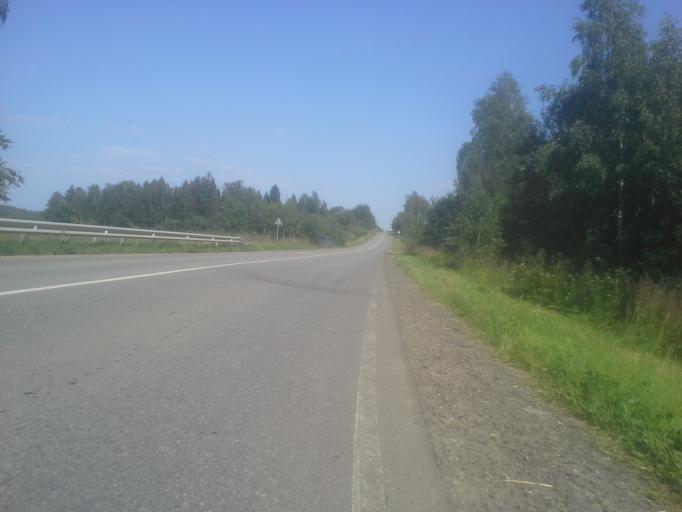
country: RU
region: Moskovskaya
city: Kolyubakino
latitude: 55.6407
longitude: 36.5844
